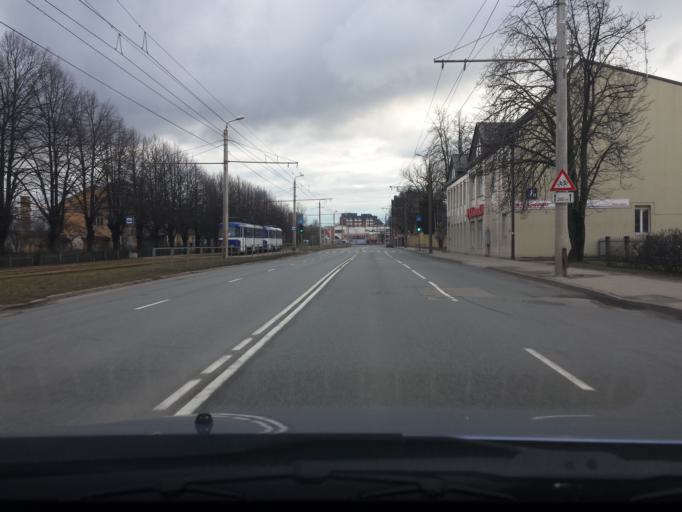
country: LV
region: Riga
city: Riga
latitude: 56.9711
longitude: 24.1088
